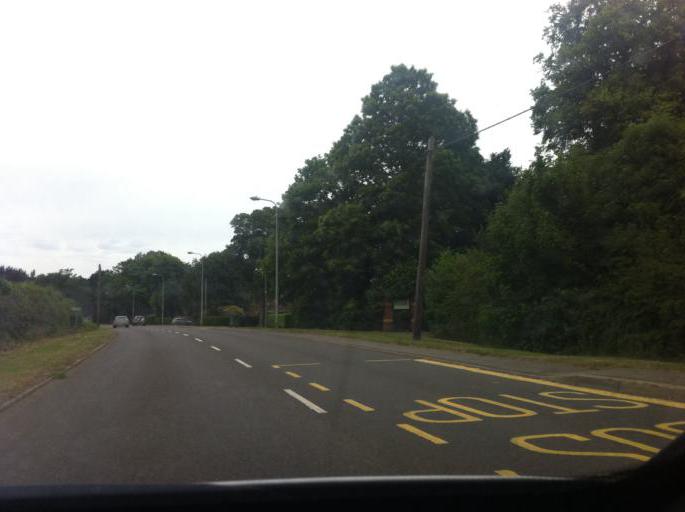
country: GB
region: England
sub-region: Northamptonshire
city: Earls Barton
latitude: 52.2707
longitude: -0.7585
